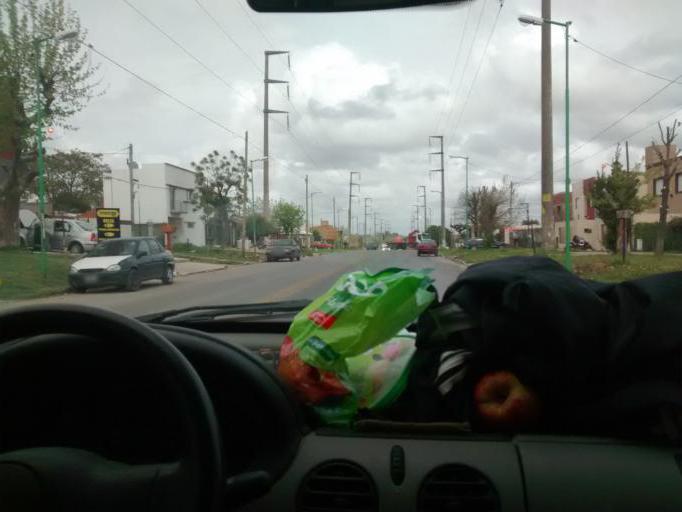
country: AR
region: Buenos Aires
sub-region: Partido de La Plata
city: La Plata
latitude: -34.9482
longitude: -57.9841
